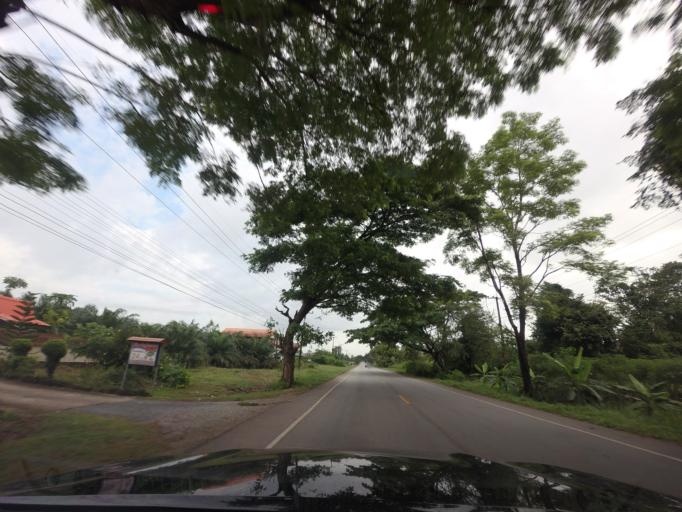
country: TH
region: Changwat Udon Thani
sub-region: Amphoe Ban Phue
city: Ban Phue
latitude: 17.7284
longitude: 102.3952
